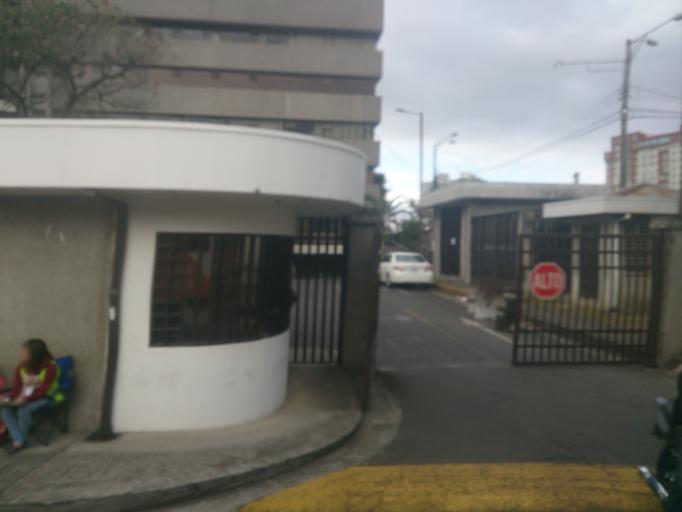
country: CR
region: San Jose
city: San Jose
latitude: 9.9312
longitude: -84.0946
